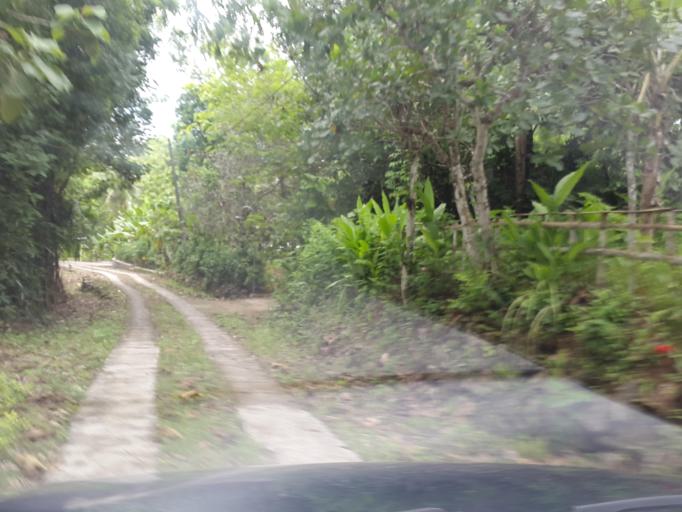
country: ID
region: Daerah Istimewa Yogyakarta
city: Wonosari
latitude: -7.8667
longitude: 110.6824
